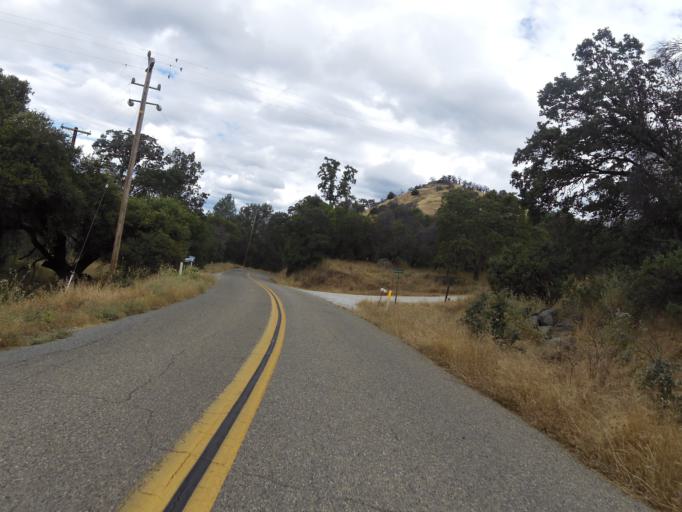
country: US
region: California
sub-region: Madera County
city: Ahwahnee
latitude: 37.3302
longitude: -119.7710
